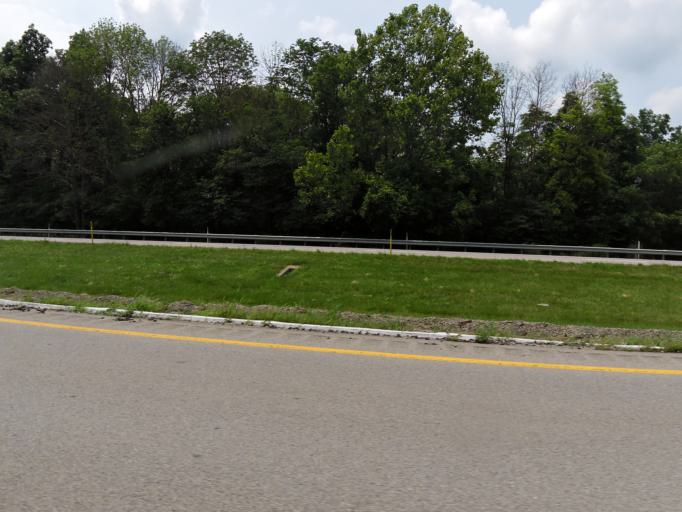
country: US
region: Kentucky
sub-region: Oldham County
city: La Grange
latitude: 38.4405
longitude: -85.3092
